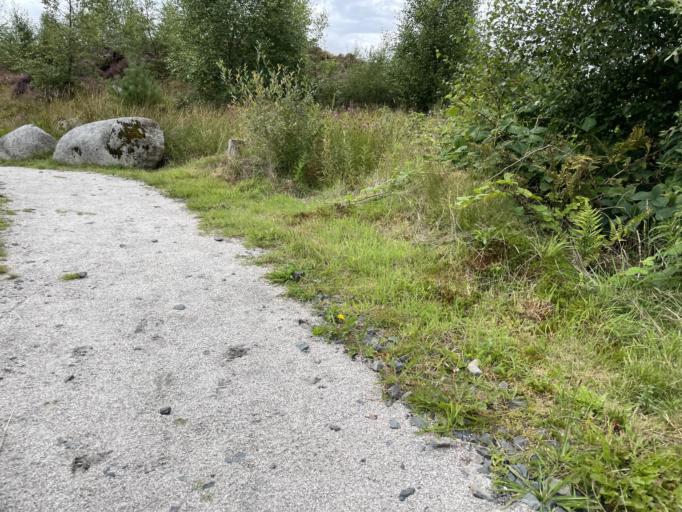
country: GB
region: Scotland
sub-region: Dumfries and Galloway
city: Newton Stewart
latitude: 55.0855
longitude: -4.5028
